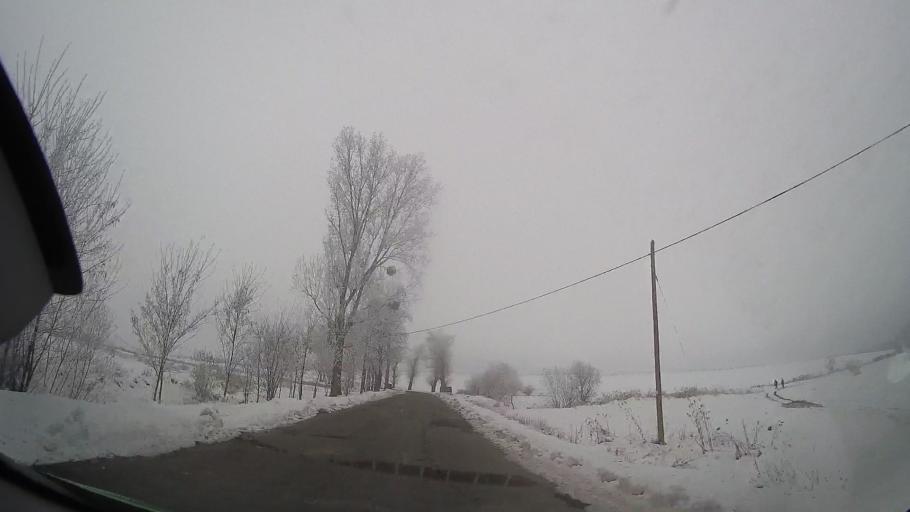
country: RO
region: Neamt
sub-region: Comuna Valea Ursului
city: Chilii
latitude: 46.8531
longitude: 27.0379
